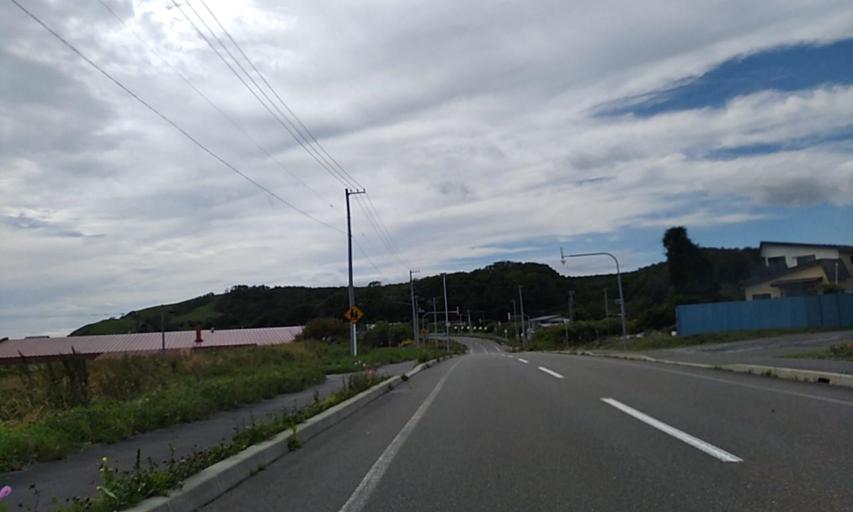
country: JP
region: Hokkaido
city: Kushiro
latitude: 42.8072
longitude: 143.8174
